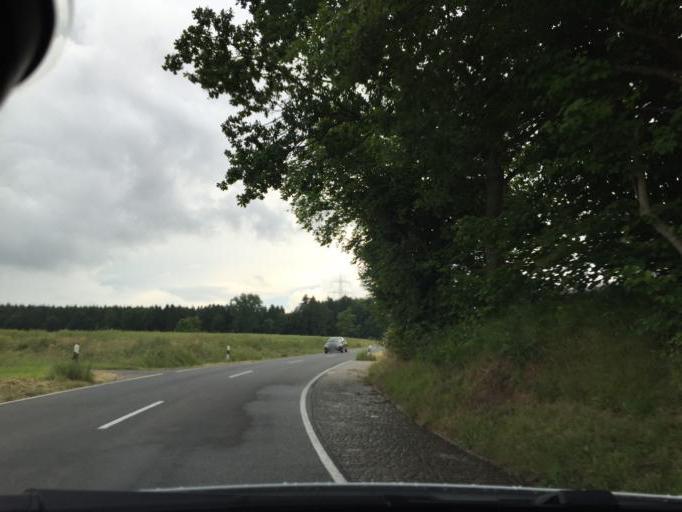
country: DE
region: Lower Saxony
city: Ottenstein
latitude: 52.0102
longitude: 9.4018
